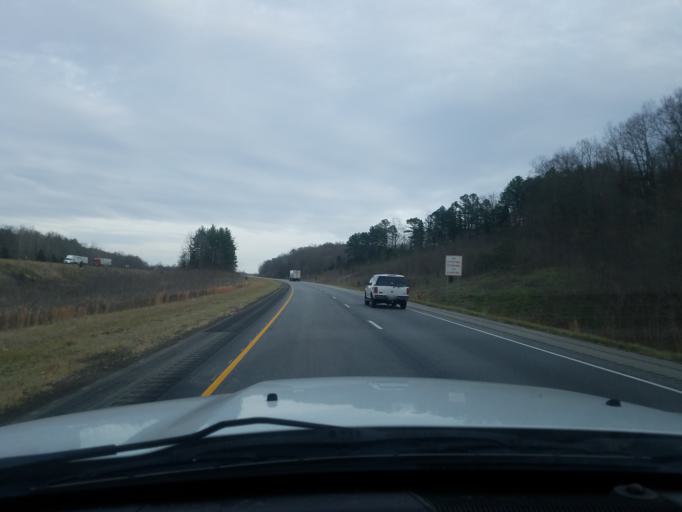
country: US
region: Indiana
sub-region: Dubois County
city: Ferdinand
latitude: 38.2303
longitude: -86.6833
